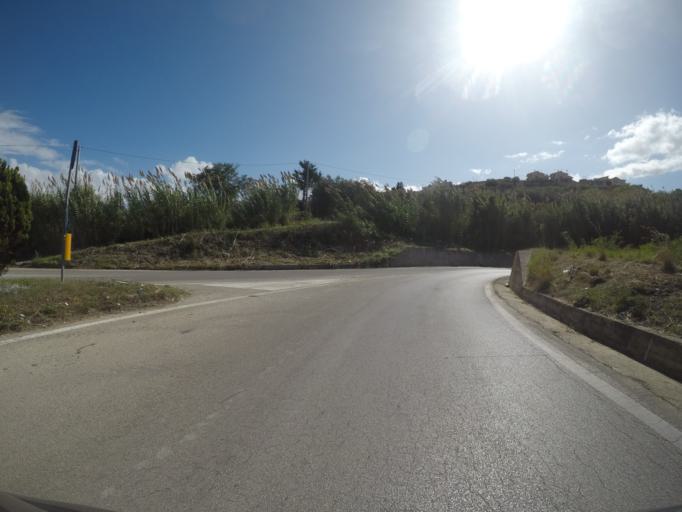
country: IT
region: Sicily
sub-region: Palermo
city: Trappeto
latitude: 38.0691
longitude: 13.0530
